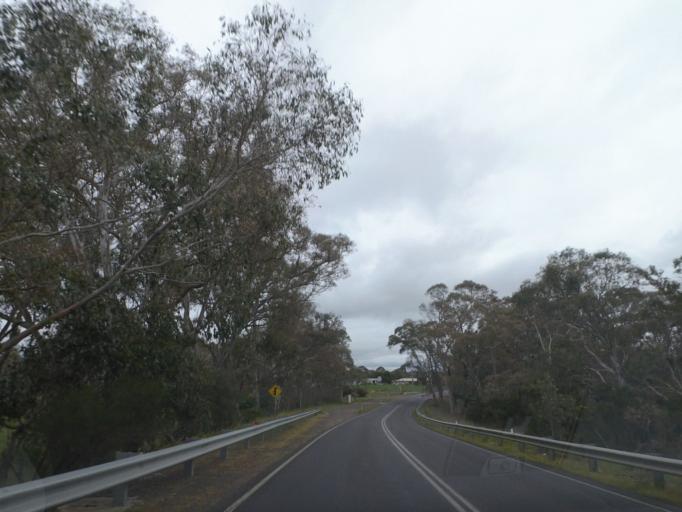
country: AU
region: Victoria
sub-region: Nillumbik
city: Doreen
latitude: -37.5706
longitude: 145.1240
